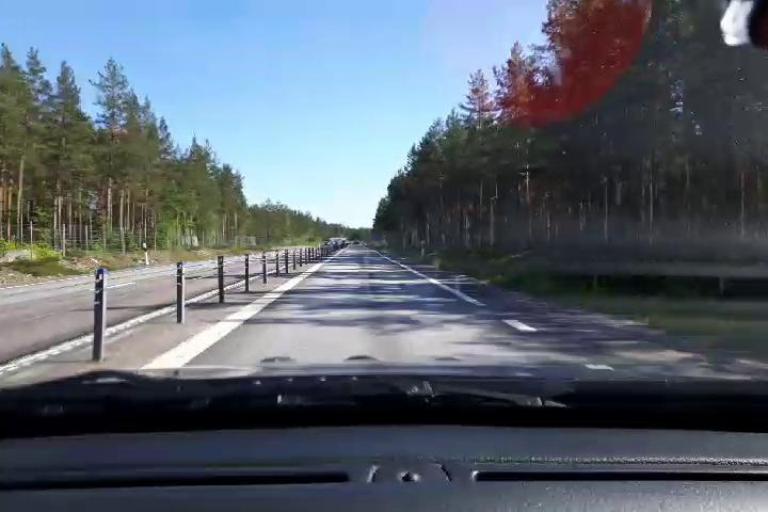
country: SE
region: Gaevleborg
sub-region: Gavle Kommun
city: Norrsundet
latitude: 60.9650
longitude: 17.0301
